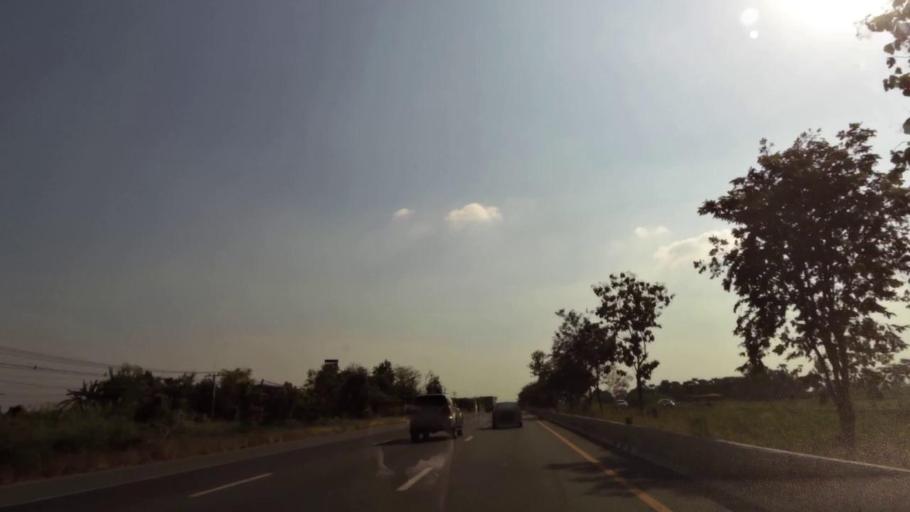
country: TH
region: Ang Thong
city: Ban Thai Tan
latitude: 14.6241
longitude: 100.4717
